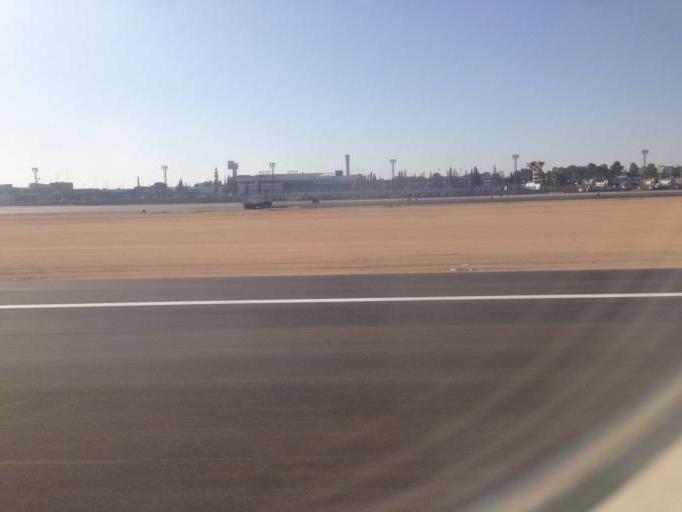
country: EG
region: Muhafazat al Qalyubiyah
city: Al Khankah
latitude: 30.1288
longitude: 31.3923
